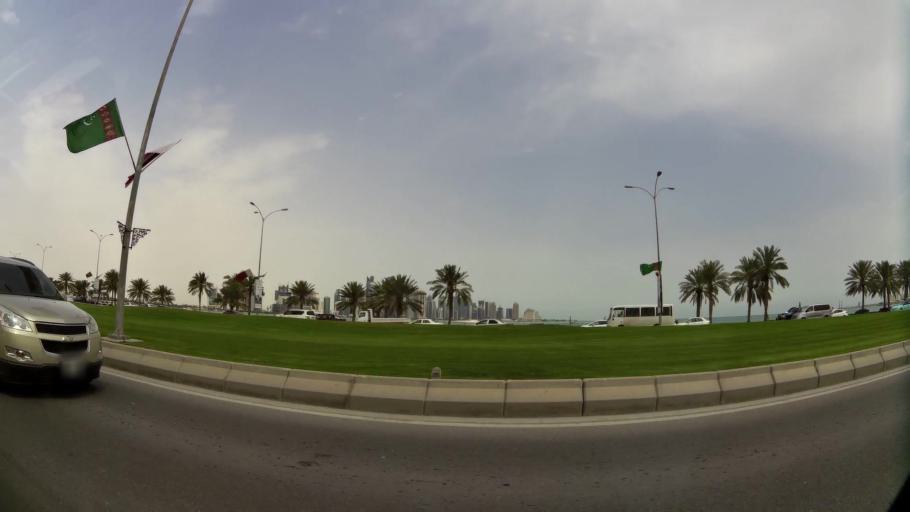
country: QA
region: Baladiyat ad Dawhah
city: Doha
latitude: 25.2945
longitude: 51.5238
